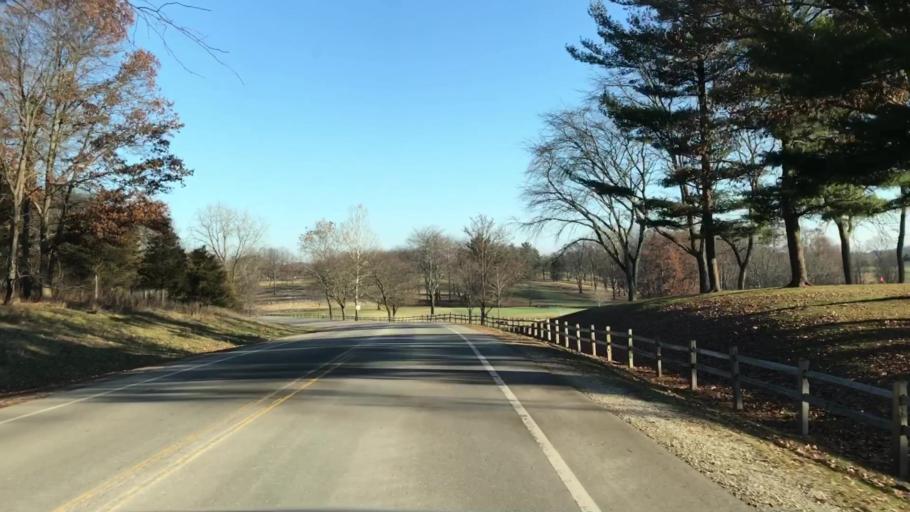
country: US
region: Michigan
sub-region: Oakland County
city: South Lyon
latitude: 42.5225
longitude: -83.6817
